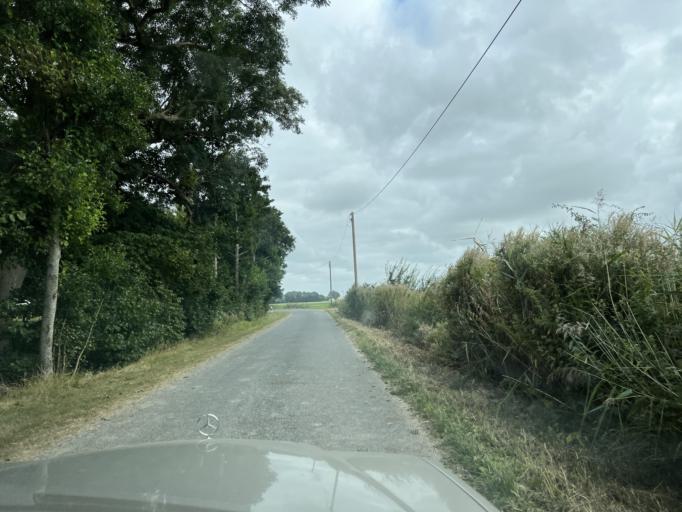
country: DE
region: Schleswig-Holstein
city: Groven
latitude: 54.2994
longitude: 8.9946
